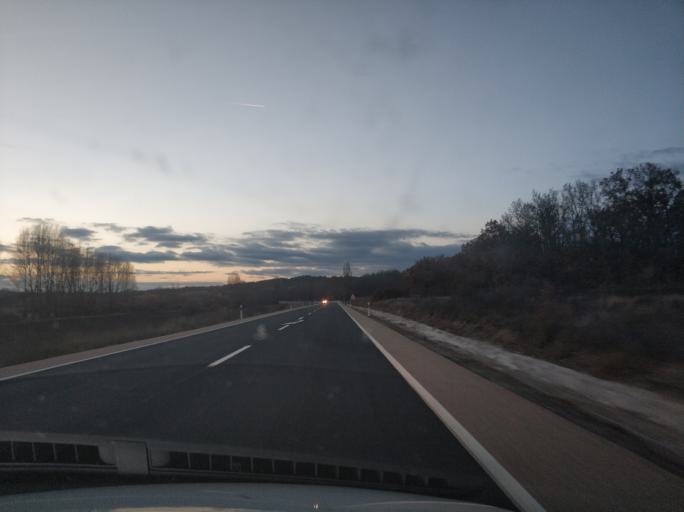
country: ES
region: Castille and Leon
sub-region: Provincia de Soria
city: Cidones
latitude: 41.8123
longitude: -2.7055
